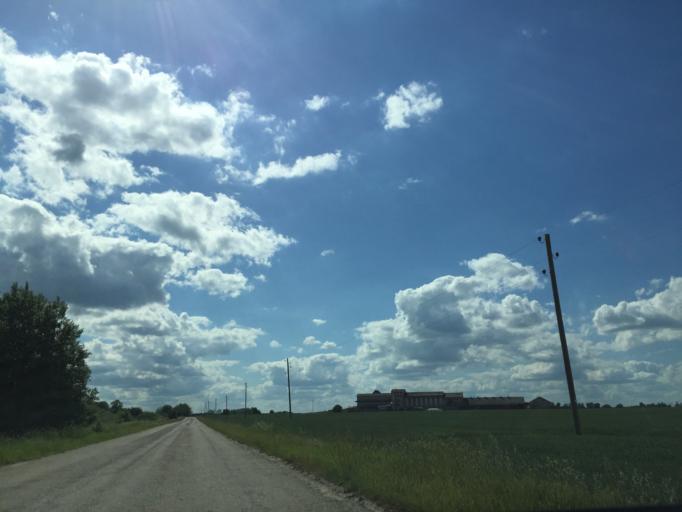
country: LV
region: Engure
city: Smarde
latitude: 56.8587
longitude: 23.3141
